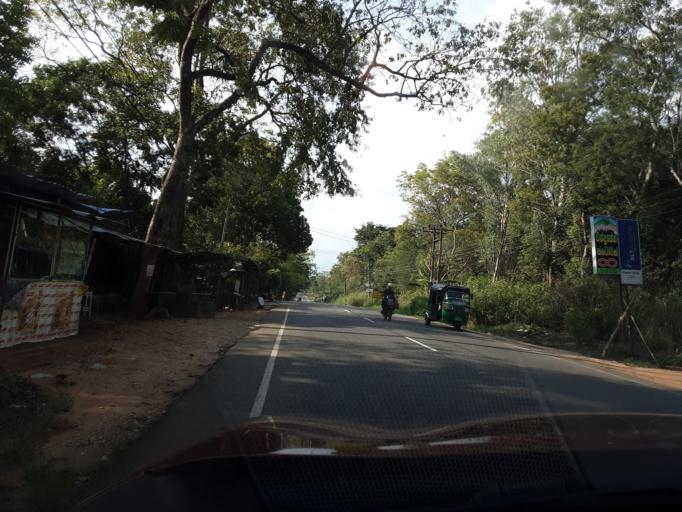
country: LK
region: Uva
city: Haputale
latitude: 6.6660
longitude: 81.1136
